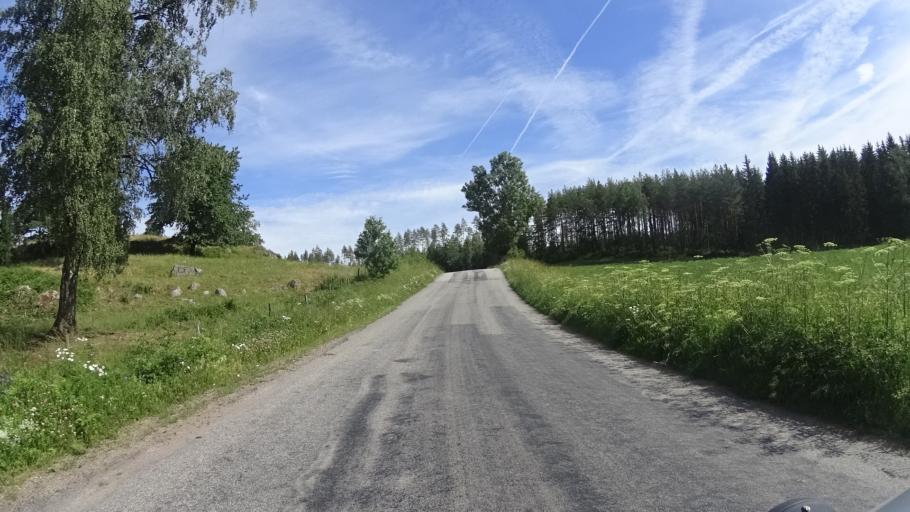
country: SE
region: Kalmar
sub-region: Vasterviks Kommun
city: Overum
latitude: 57.8776
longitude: 16.1758
